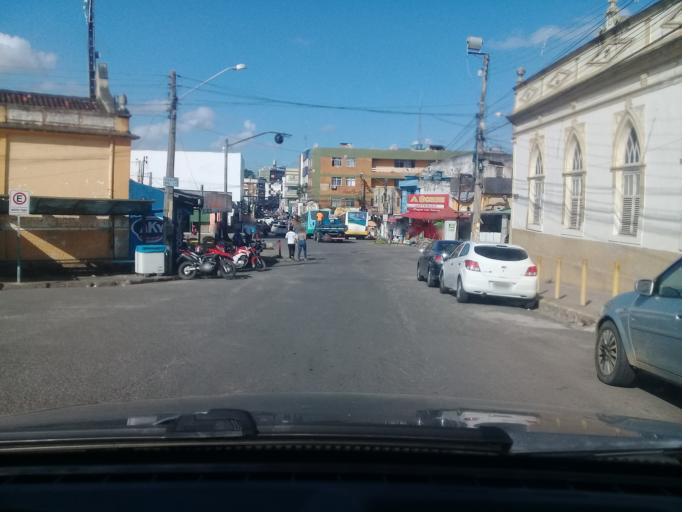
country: BR
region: Pernambuco
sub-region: Vitoria De Santo Antao
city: Vitoria de Santo Antao
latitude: -8.1206
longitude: -35.2970
